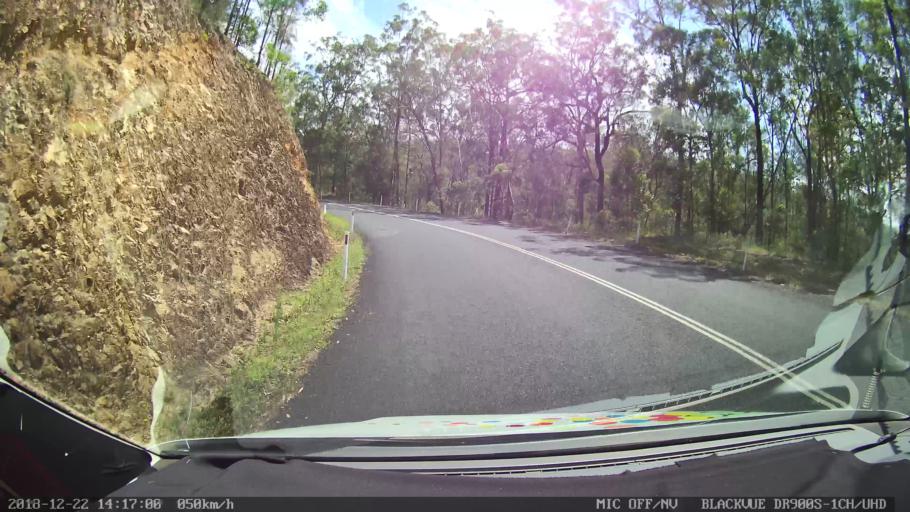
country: AU
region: New South Wales
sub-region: Clarence Valley
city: Coutts Crossing
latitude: -30.0059
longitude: 152.6688
